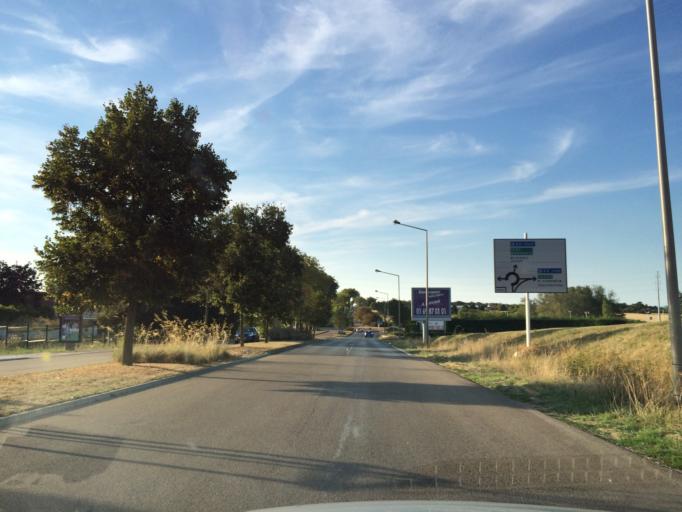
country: FR
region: Bourgogne
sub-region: Departement de l'Yonne
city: Auxerre
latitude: 47.8139
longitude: 3.5616
